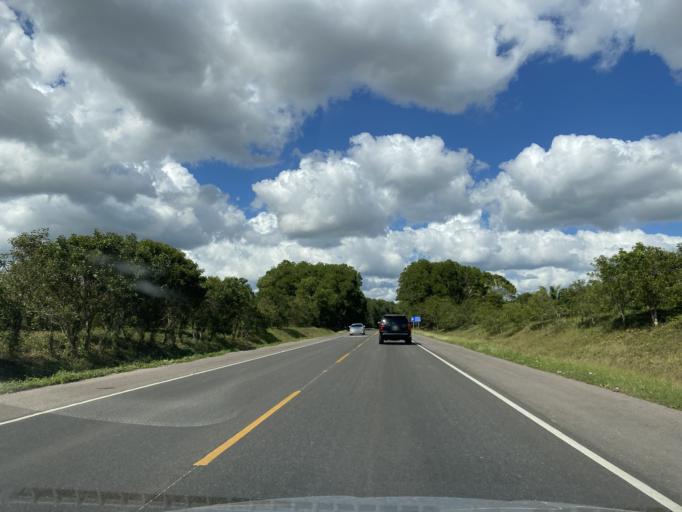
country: DO
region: Monte Plata
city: Monte Plata
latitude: 18.7467
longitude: -69.7654
